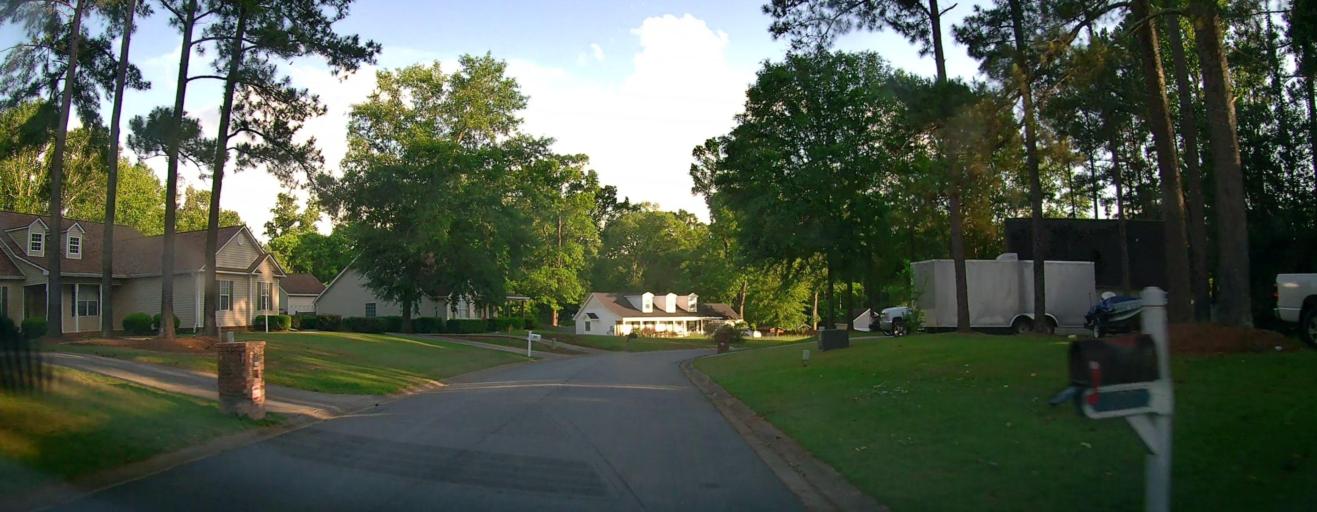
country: US
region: Georgia
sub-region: Houston County
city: Centerville
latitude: 32.6398
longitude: -83.7143
